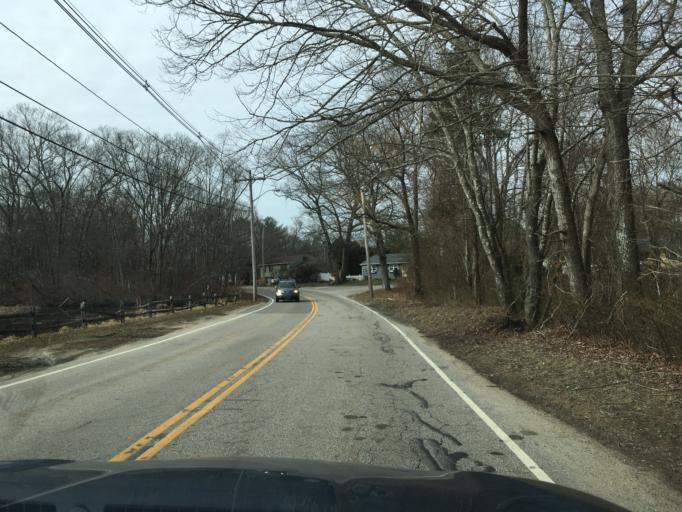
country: US
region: Rhode Island
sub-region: Kent County
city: East Greenwich
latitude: 41.6294
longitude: -71.4470
